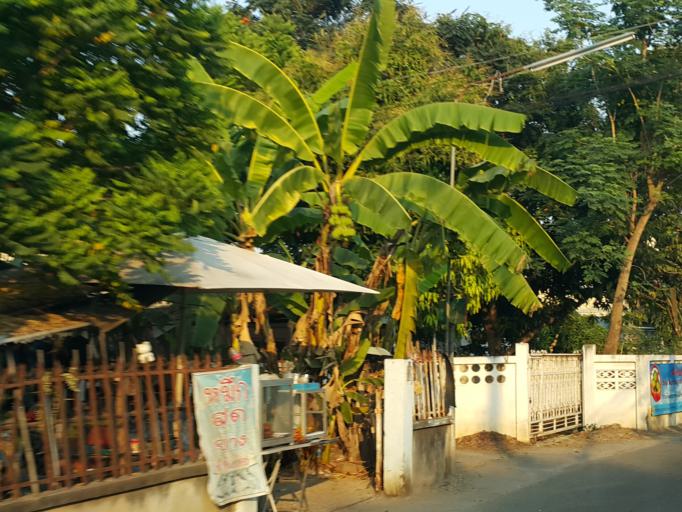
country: TH
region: Chiang Mai
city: San Sai
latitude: 18.9113
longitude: 98.9277
